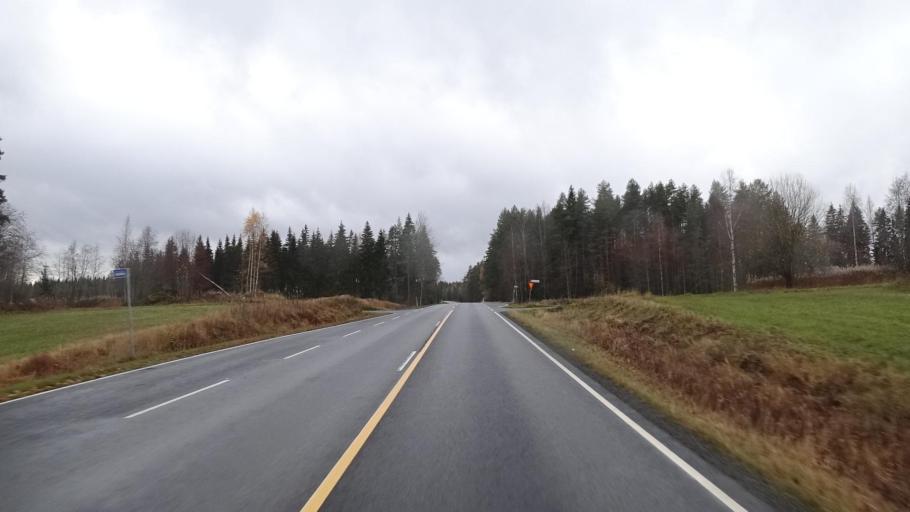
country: FI
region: Southern Savonia
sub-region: Mikkeli
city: Kangasniemi
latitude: 62.1610
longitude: 26.8325
